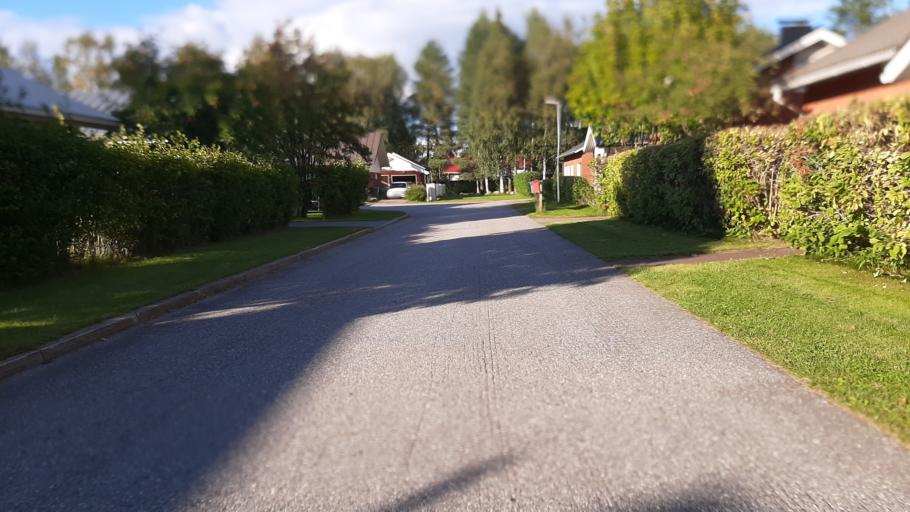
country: FI
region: North Karelia
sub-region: Joensuu
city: Joensuu
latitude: 62.6240
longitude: 29.7990
